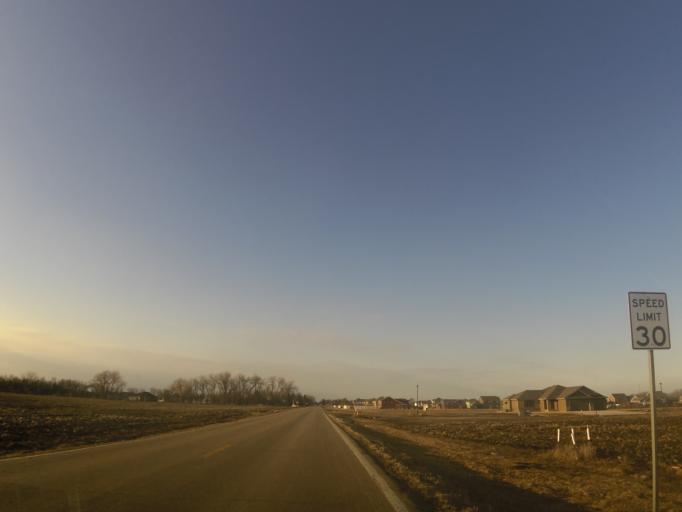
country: US
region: North Dakota
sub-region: Grand Forks County
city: Grand Forks
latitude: 47.8614
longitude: -97.0291
